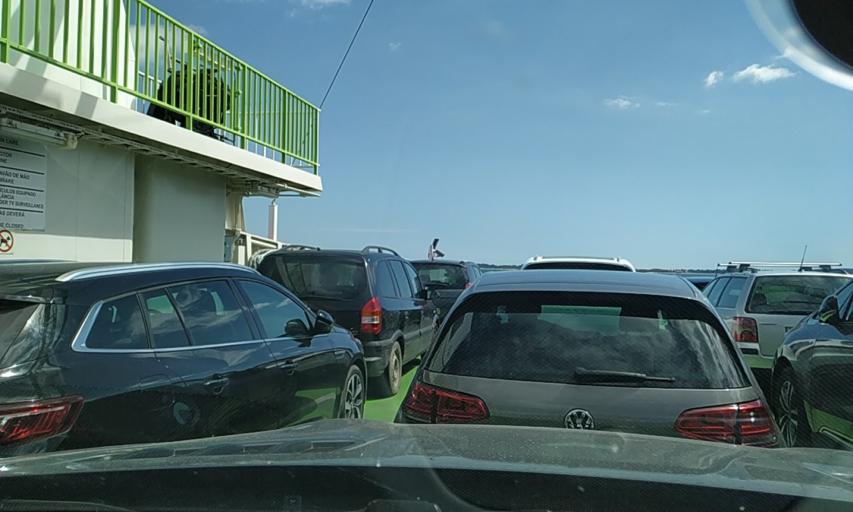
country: PT
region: Setubal
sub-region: Setubal
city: Setubal
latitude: 38.5102
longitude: -8.8852
